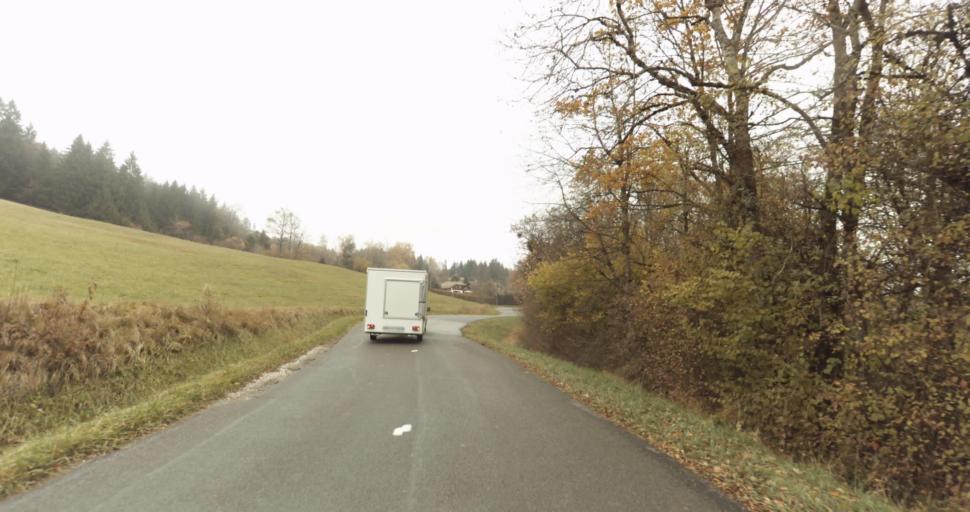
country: FR
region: Rhone-Alpes
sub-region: Departement de la Haute-Savoie
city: Groisy
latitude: 46.0217
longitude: 6.1785
